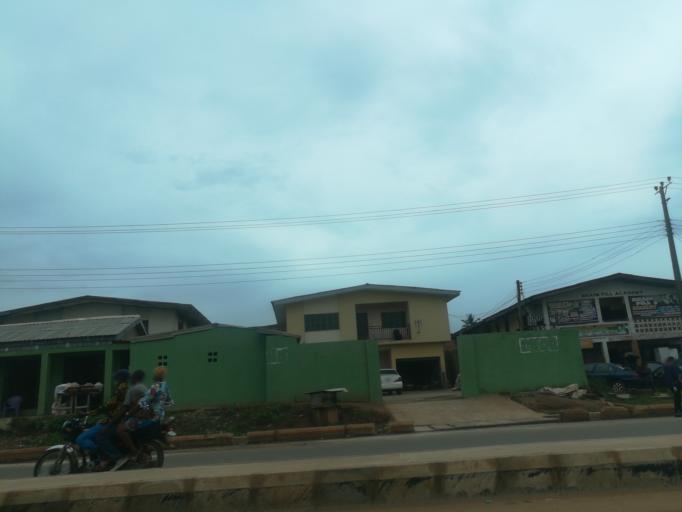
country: NG
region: Oyo
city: Ibadan
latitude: 7.3914
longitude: 3.9426
